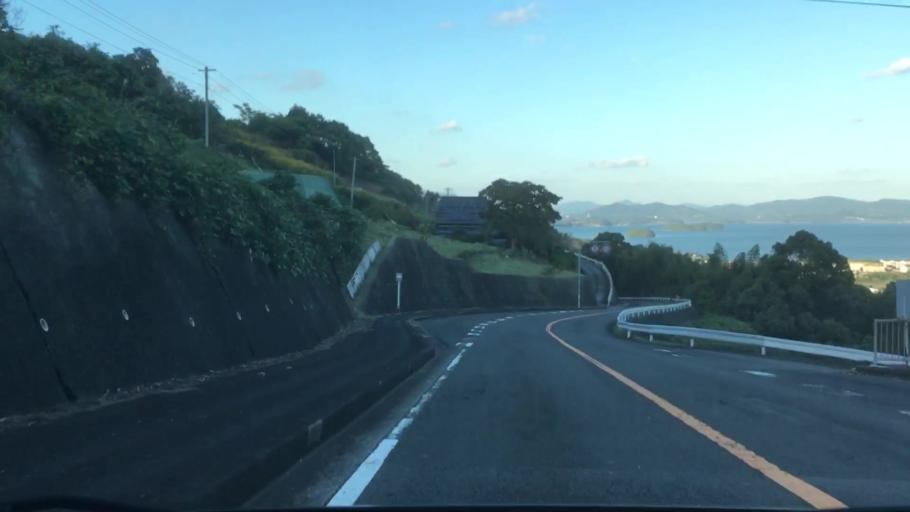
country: JP
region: Nagasaki
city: Sasebo
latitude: 32.9956
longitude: 129.7246
